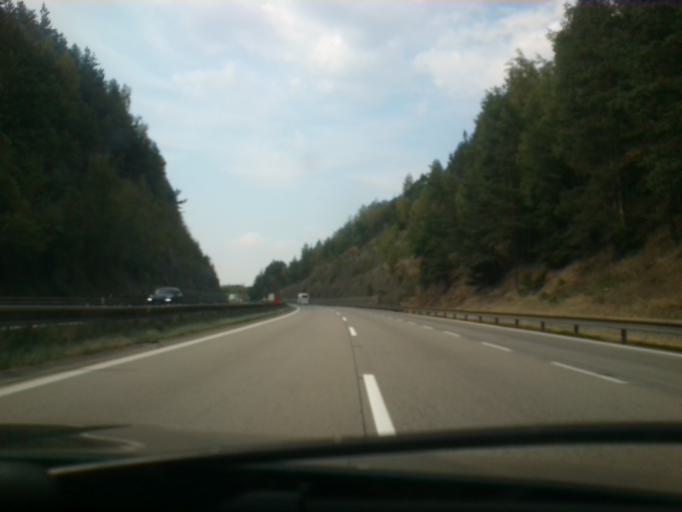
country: CZ
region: Central Bohemia
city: Ondrejov
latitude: 49.8852
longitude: 14.7564
